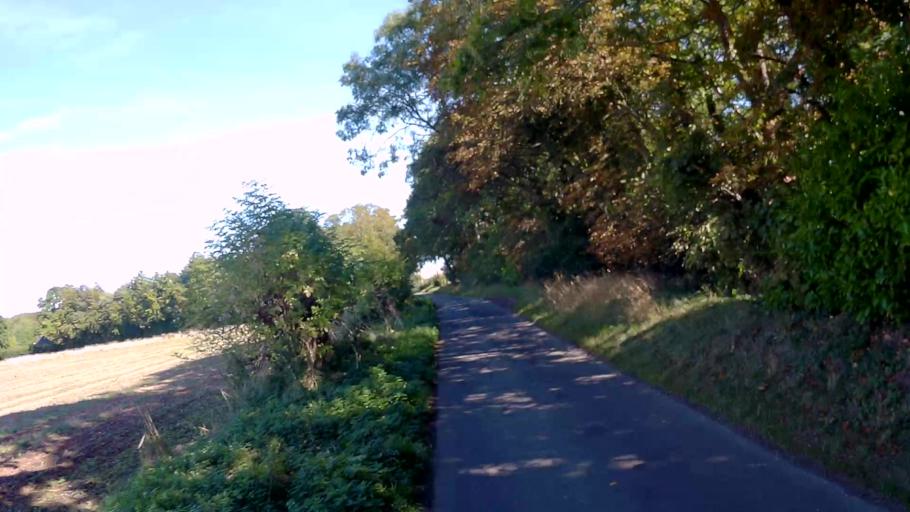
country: GB
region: England
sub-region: Hampshire
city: Andover
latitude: 51.1613
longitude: -1.4189
